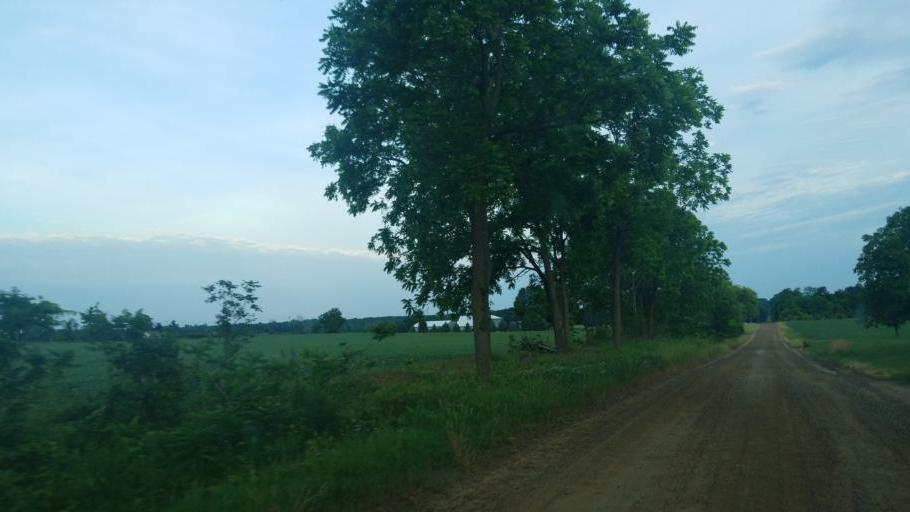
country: US
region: Michigan
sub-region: Eaton County
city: Charlotte
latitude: 42.5972
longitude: -84.8912
